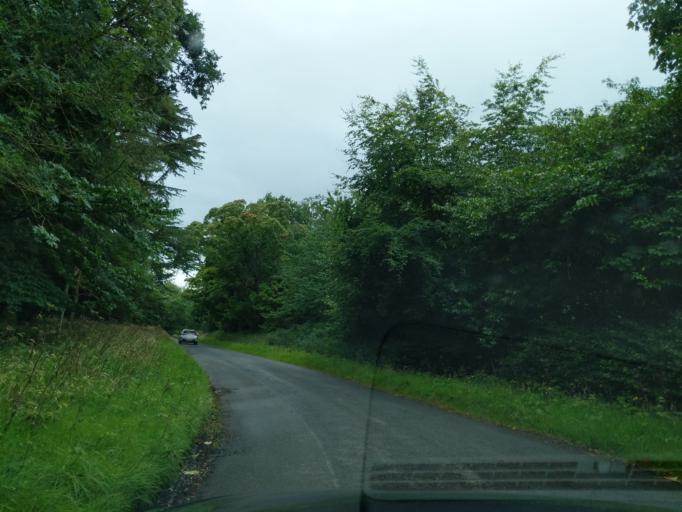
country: GB
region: Scotland
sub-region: Fife
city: Limekilns
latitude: 55.9926
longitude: -3.4802
